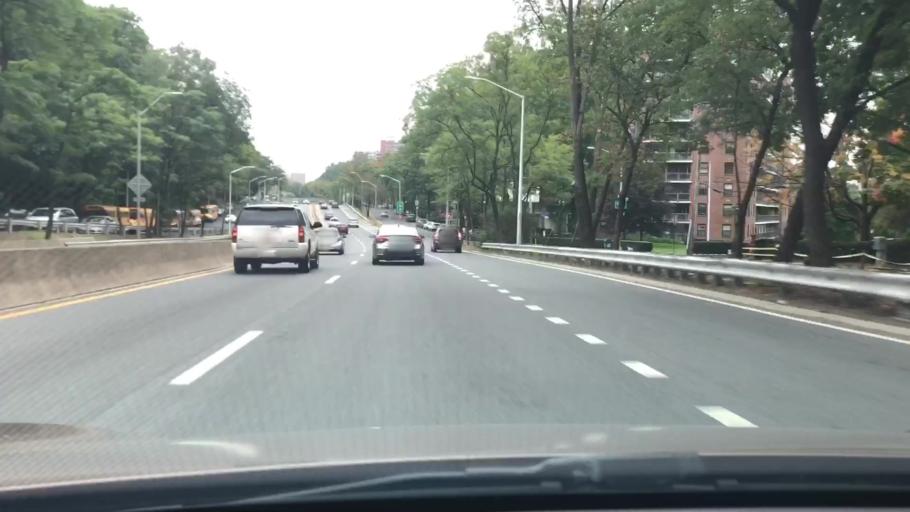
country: US
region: New York
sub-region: Westchester County
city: Yonkers
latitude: 40.8978
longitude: -73.9080
